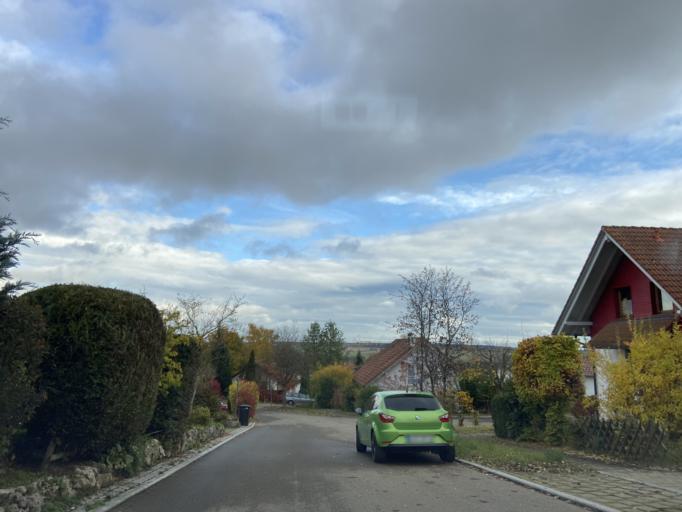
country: DE
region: Baden-Wuerttemberg
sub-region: Tuebingen Region
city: Inzigkofen
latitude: 48.0702
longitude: 9.1711
